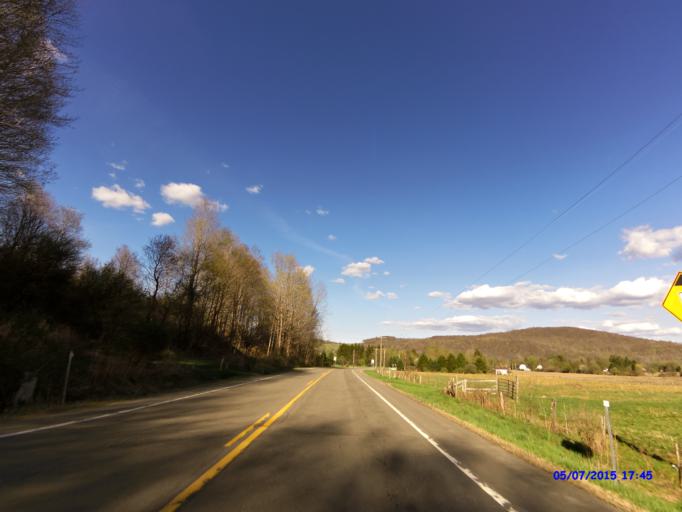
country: US
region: New York
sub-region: Cattaraugus County
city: Franklinville
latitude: 42.3204
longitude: -78.4748
